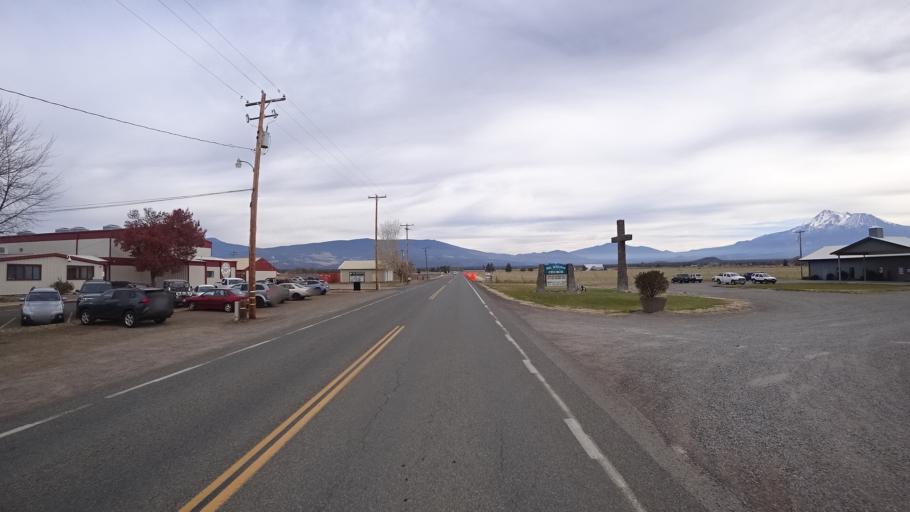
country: US
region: California
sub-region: Siskiyou County
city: Montague
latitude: 41.6240
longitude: -122.4059
